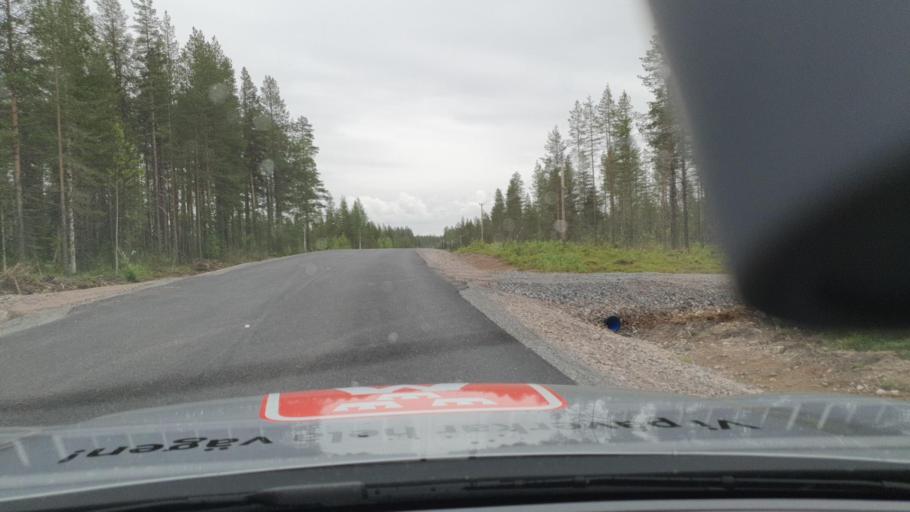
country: SE
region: Norrbotten
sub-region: Overtornea Kommun
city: OEvertornea
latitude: 66.6506
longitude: 23.2348
